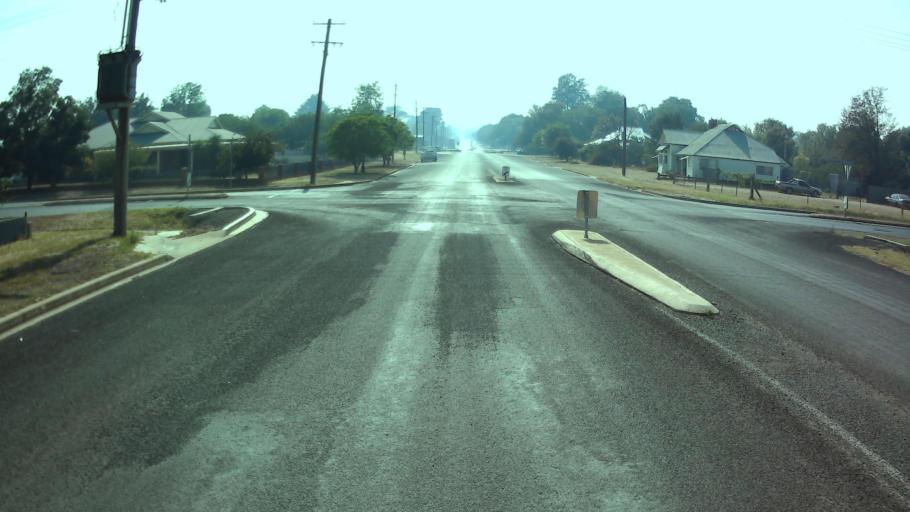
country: AU
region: New South Wales
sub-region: Weddin
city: Grenfell
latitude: -33.8919
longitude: 148.1568
